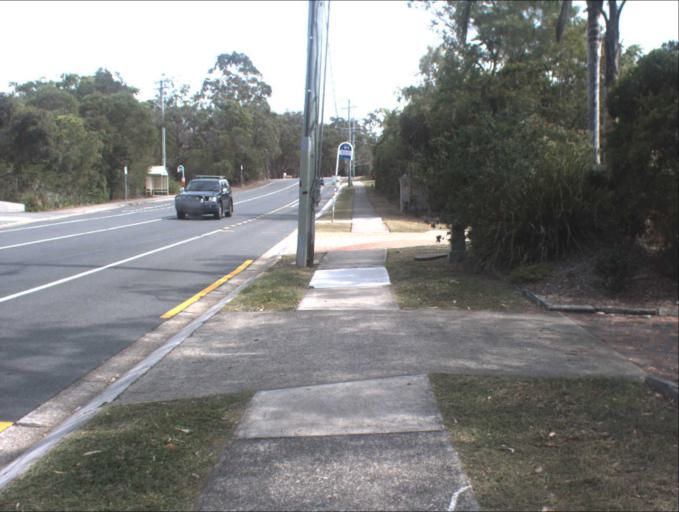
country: AU
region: Queensland
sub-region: Logan
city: Springwood
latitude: -27.6263
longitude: 153.1474
